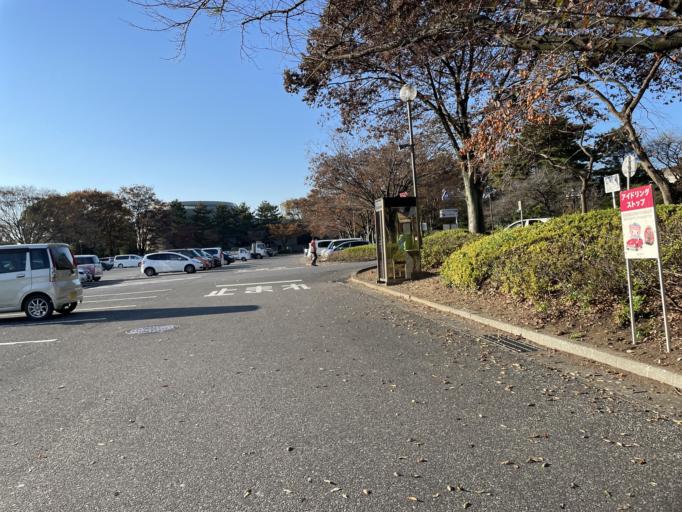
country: JP
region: Gunma
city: Tatebayashi
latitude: 36.2437
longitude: 139.5418
